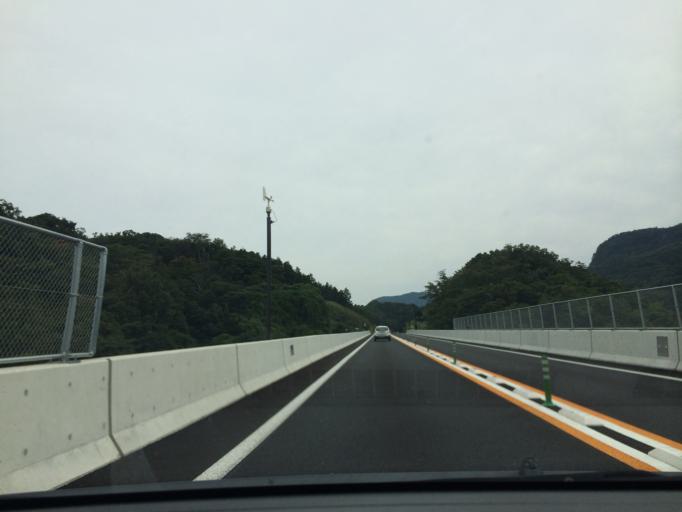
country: JP
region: Shimane
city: Gotsucho
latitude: 35.0888
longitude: 132.3598
